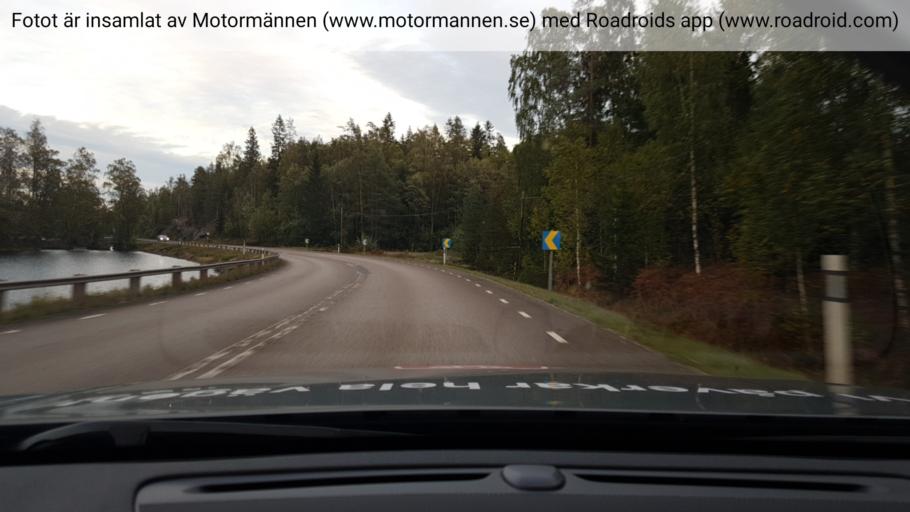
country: SE
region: Vaestra Goetaland
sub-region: Amals Kommun
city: Amal
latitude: 59.0776
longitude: 12.5996
